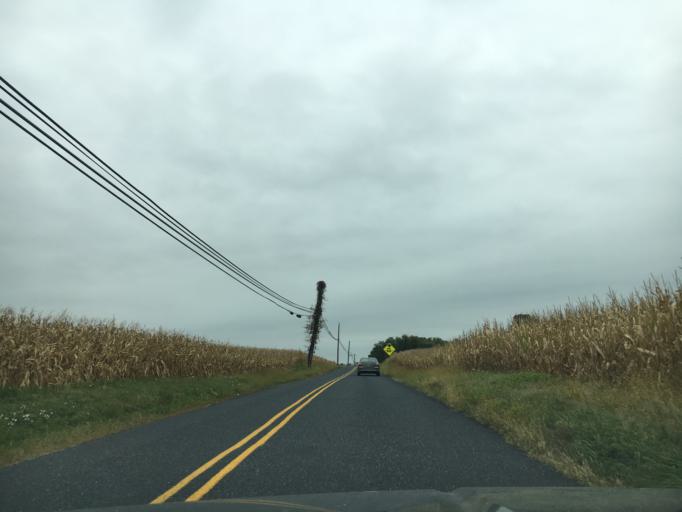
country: US
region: Pennsylvania
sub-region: Northampton County
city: Bath
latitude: 40.6966
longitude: -75.4073
